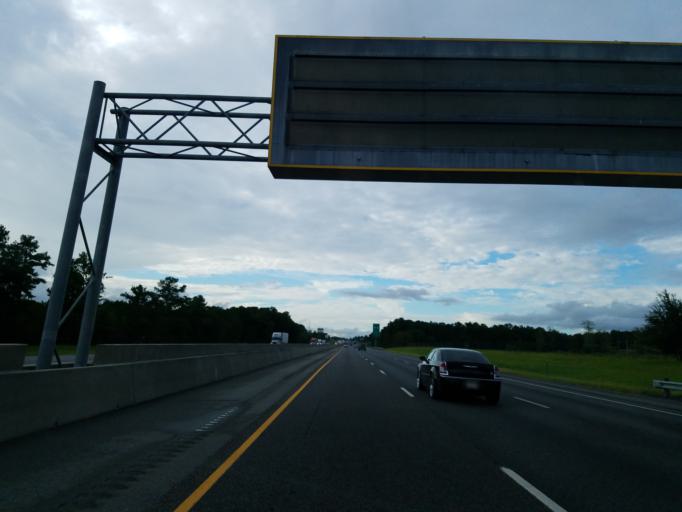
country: US
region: Georgia
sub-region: Lowndes County
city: Hahira
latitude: 30.9735
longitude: -83.3822
